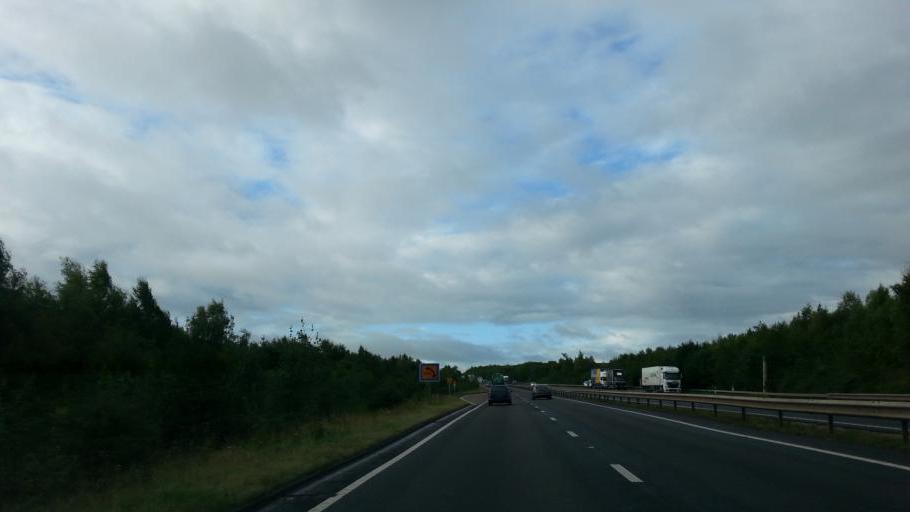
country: GB
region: England
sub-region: Leicestershire
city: Ashby de la Zouch
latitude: 52.7671
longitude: -1.4282
